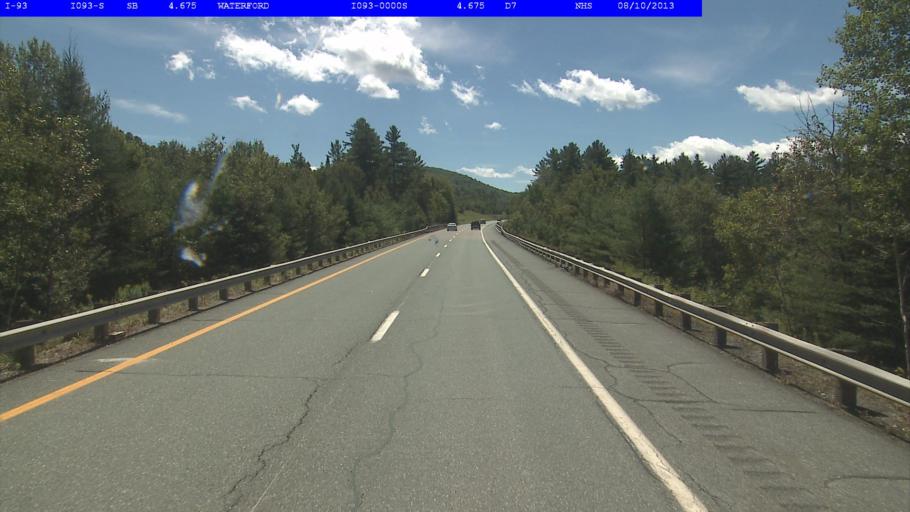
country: US
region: Vermont
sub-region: Caledonia County
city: Saint Johnsbury
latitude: 44.4030
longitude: -71.9194
